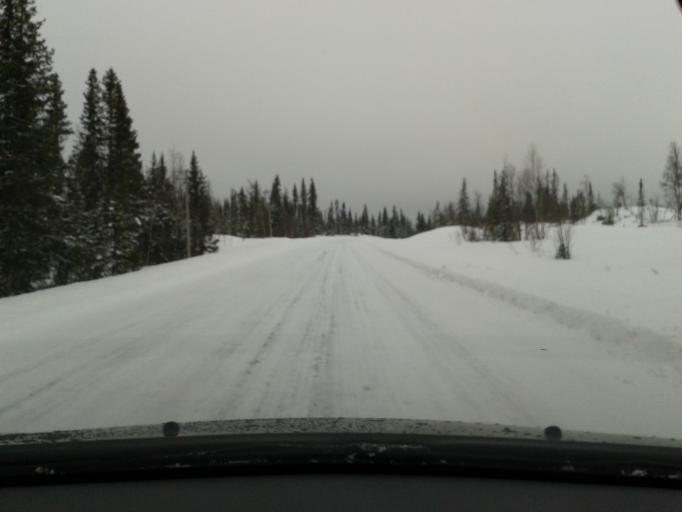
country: SE
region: Vaesterbotten
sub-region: Vilhelmina Kommun
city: Sjoberg
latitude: 65.1457
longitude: 15.8689
